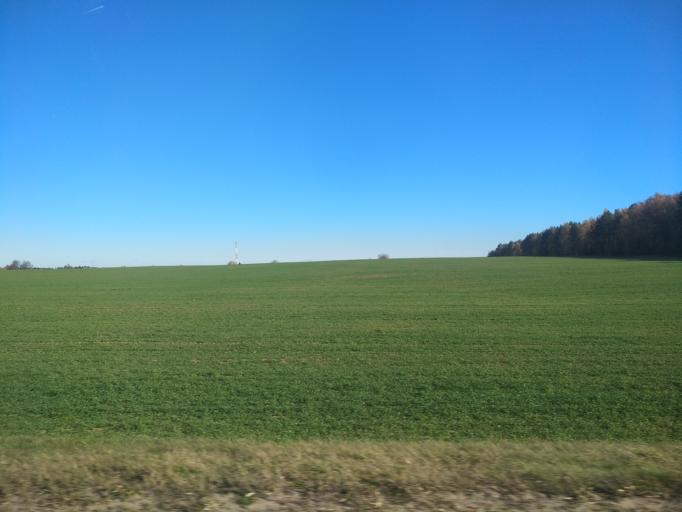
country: BY
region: Minsk
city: Kryvichy
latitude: 54.5823
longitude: 27.1978
